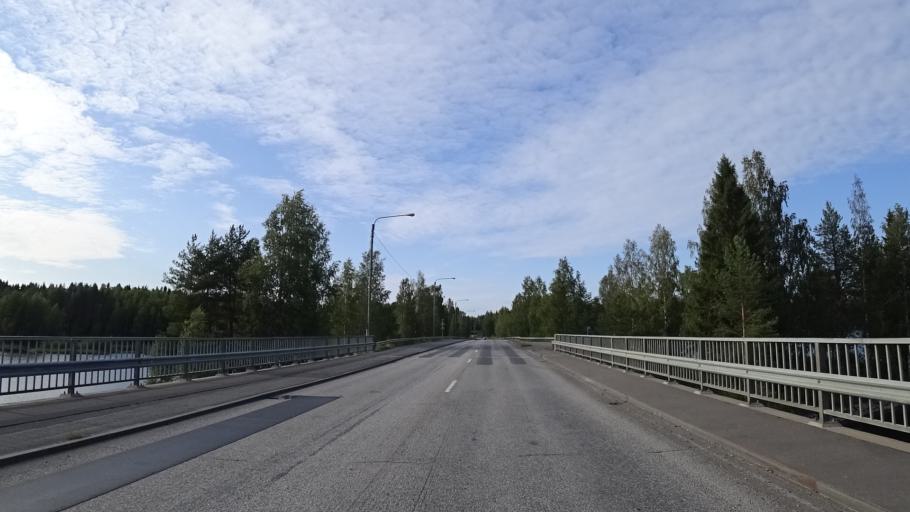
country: FI
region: North Karelia
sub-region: Joensuu
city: Eno
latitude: 62.8030
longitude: 30.1533
